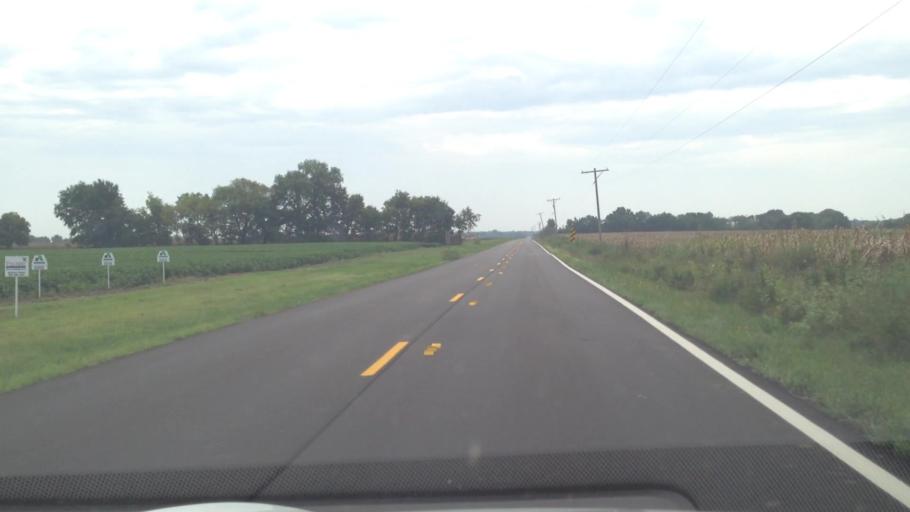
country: US
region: Kansas
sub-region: Crawford County
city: Girard
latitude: 37.6272
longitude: -94.9698
